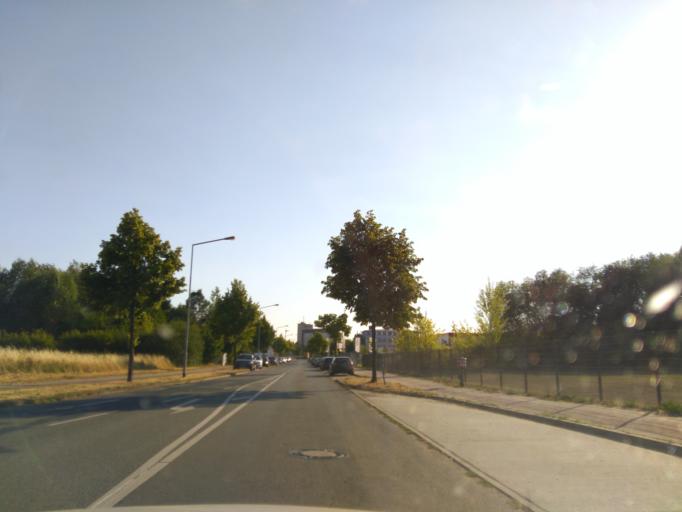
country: DE
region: Brandenburg
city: Nauen
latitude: 52.5987
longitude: 12.8908
